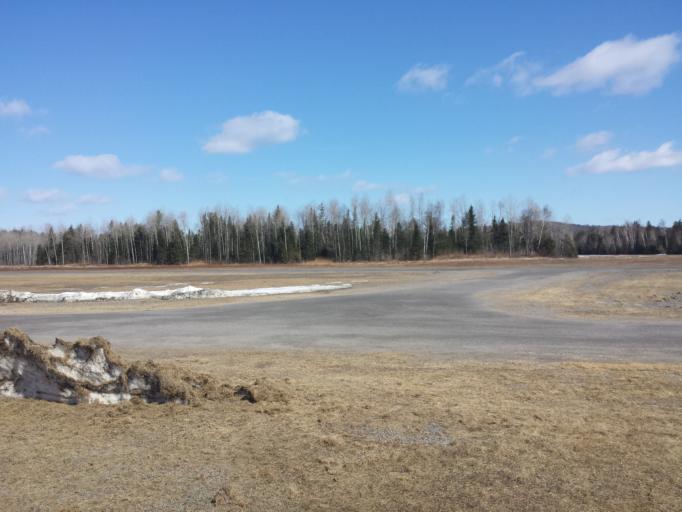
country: CA
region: Ontario
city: Bancroft
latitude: 45.0718
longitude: -77.8800
